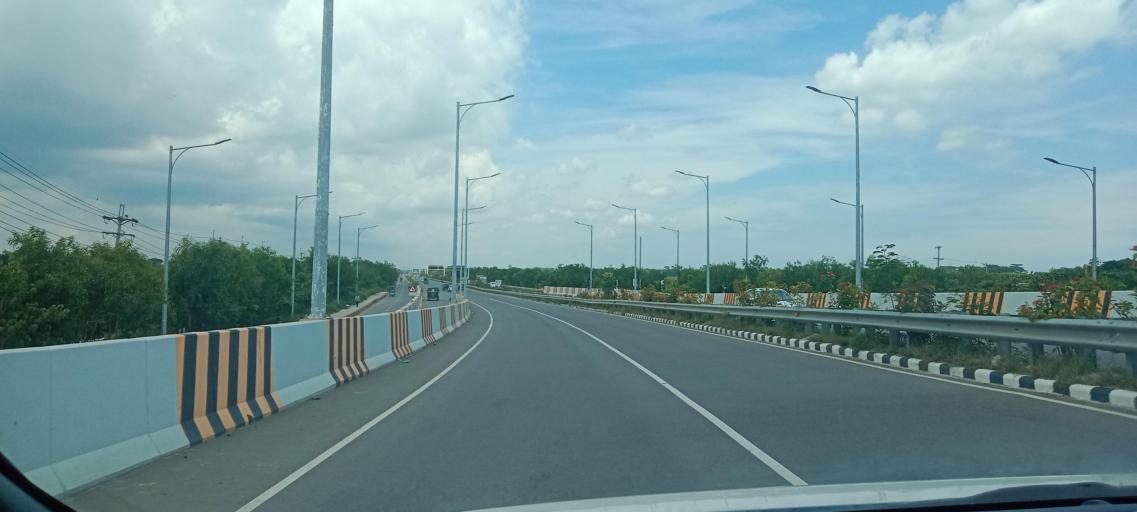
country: BD
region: Dhaka
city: Char Bhadrasan
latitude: 23.3709
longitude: 90.0351
